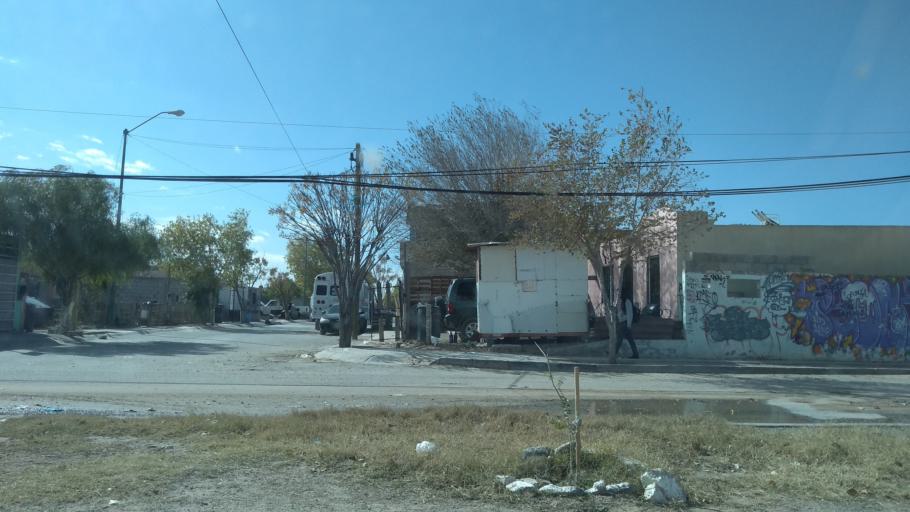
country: US
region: Texas
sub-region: El Paso County
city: Socorro Mission Number 1 Colonia
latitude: 31.5859
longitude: -106.3578
